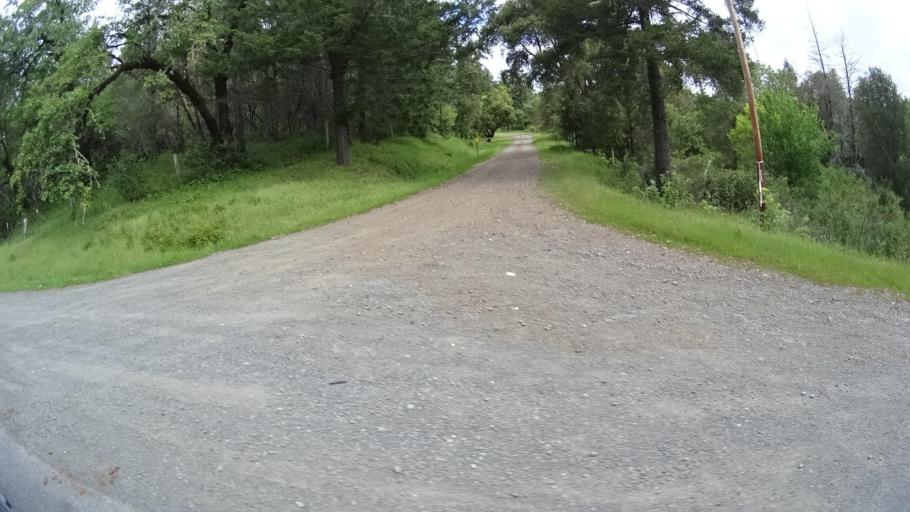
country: US
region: California
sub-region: Humboldt County
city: Redway
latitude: 40.1853
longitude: -123.5884
